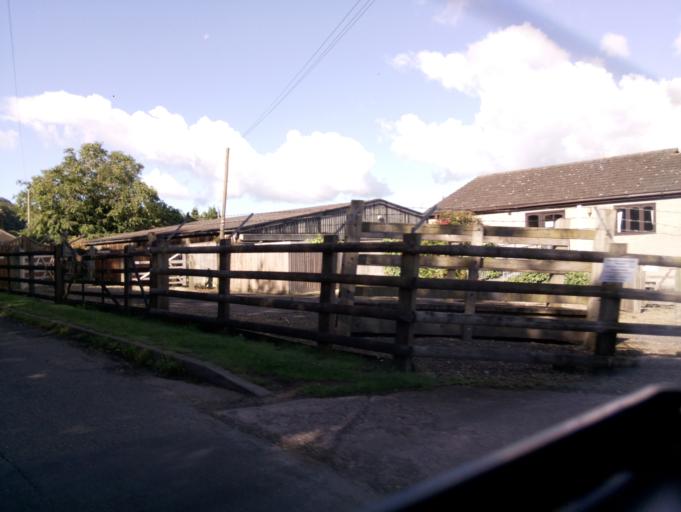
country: GB
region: England
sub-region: Herefordshire
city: Walford
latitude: 51.8755
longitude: -2.6017
